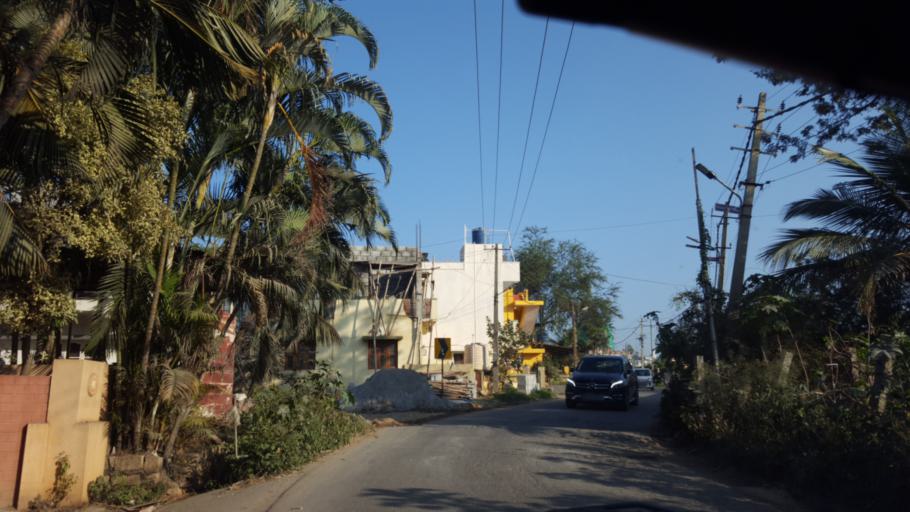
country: IN
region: Karnataka
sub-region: Bangalore Rural
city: Hoskote
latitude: 12.9165
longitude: 77.7645
